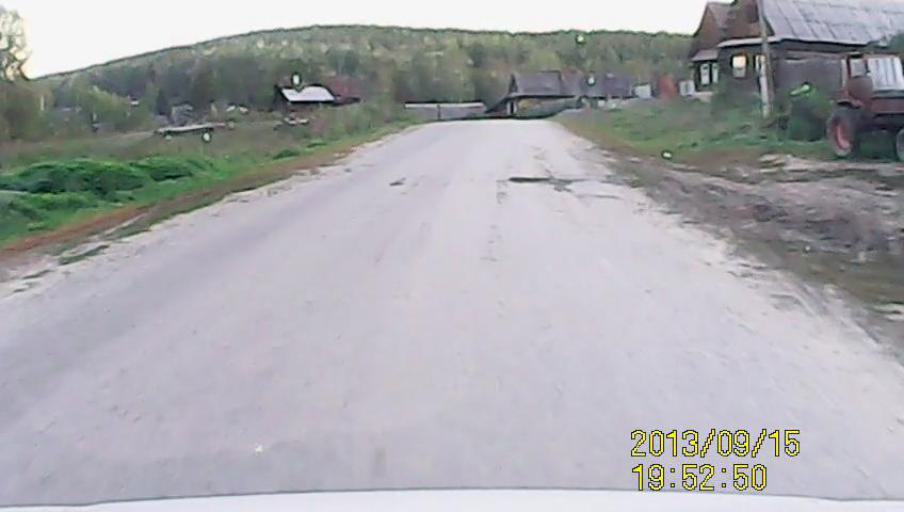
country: RU
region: Chelyabinsk
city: Kyshtym
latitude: 55.7665
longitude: 60.4865
